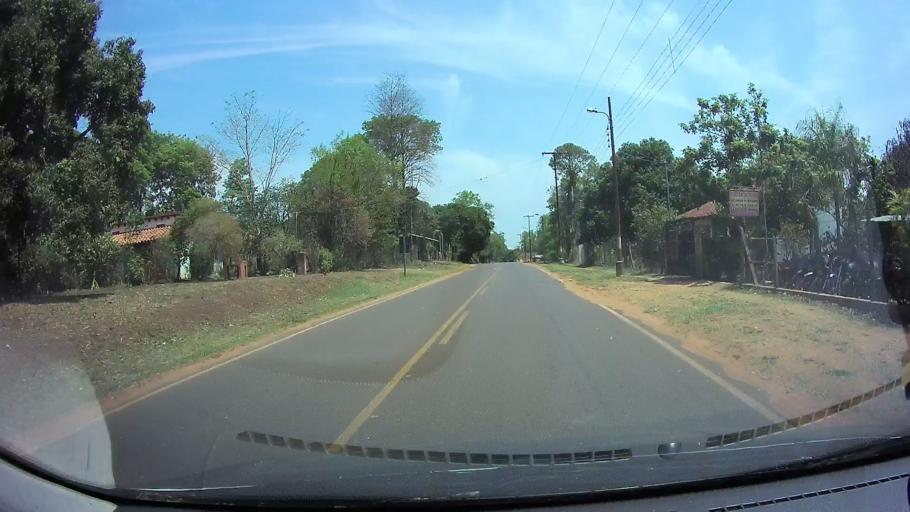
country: PY
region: Central
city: Ita
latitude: -25.4361
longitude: -57.3979
